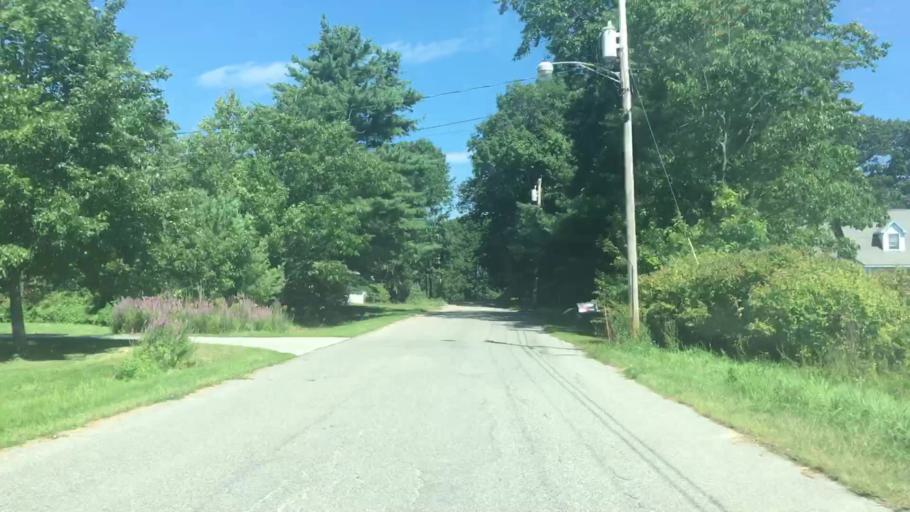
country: US
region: Maine
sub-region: Androscoggin County
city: Sabattus
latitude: 44.1029
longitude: -70.1276
